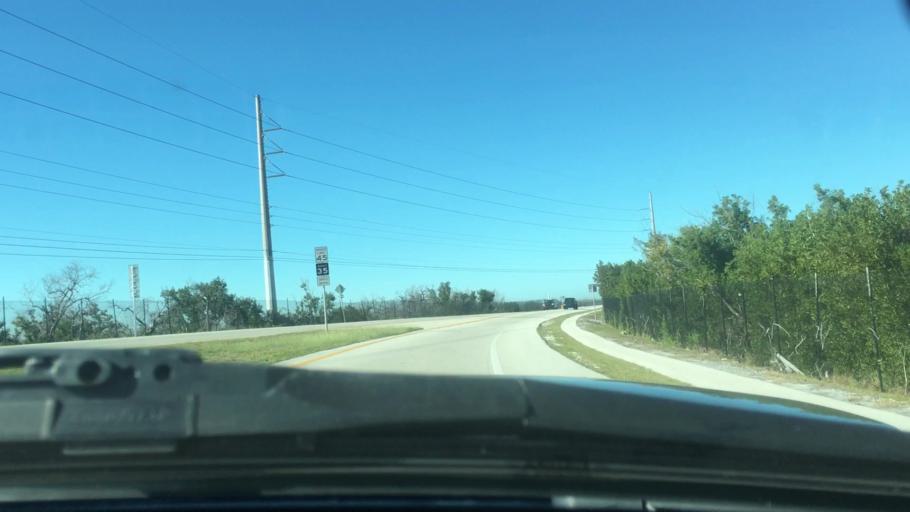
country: US
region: Florida
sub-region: Monroe County
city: Big Pine Key
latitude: 24.6501
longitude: -81.3335
